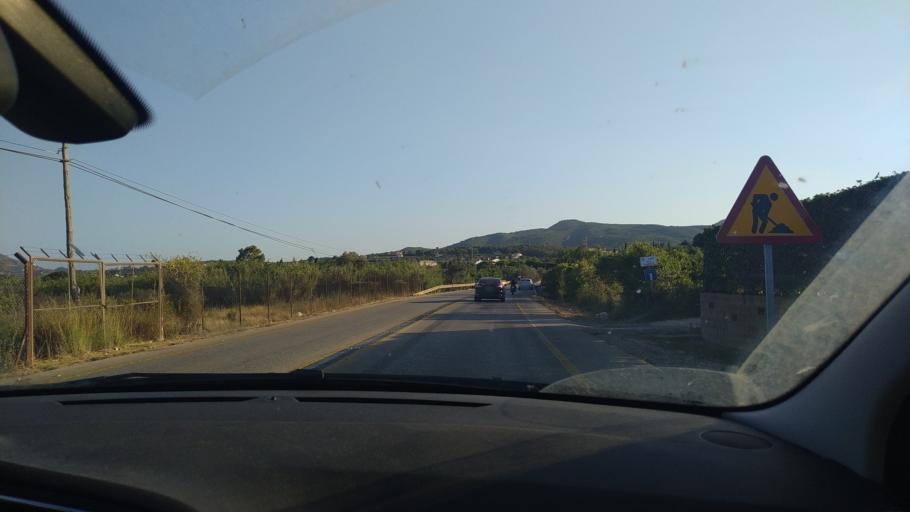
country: ES
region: Valencia
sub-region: Provincia de Alicante
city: Javea
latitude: 38.7771
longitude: 0.1467
